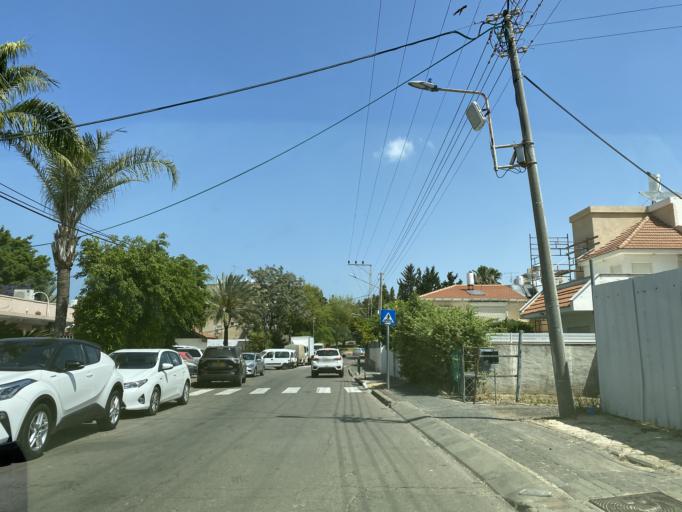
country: IL
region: Tel Aviv
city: Ramat HaSharon
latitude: 32.1553
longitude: 34.8365
